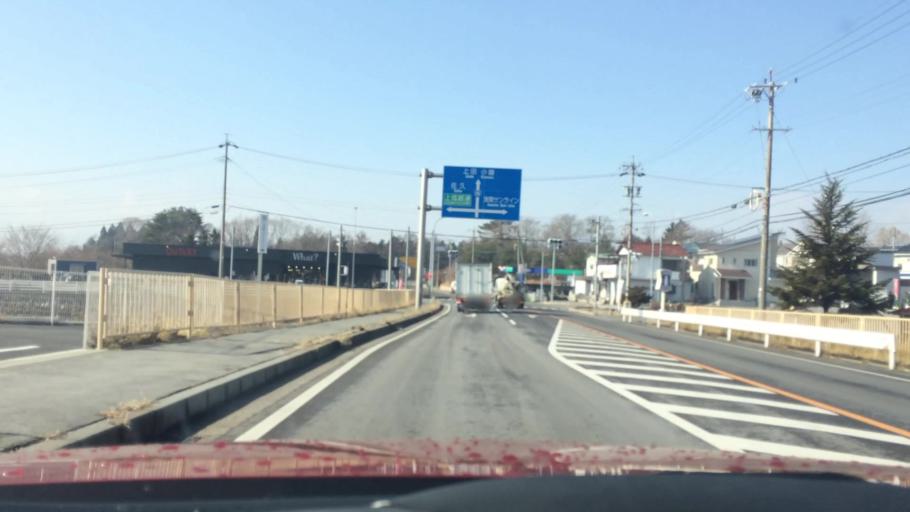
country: JP
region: Nagano
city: Komoro
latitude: 36.3280
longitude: 138.5099
